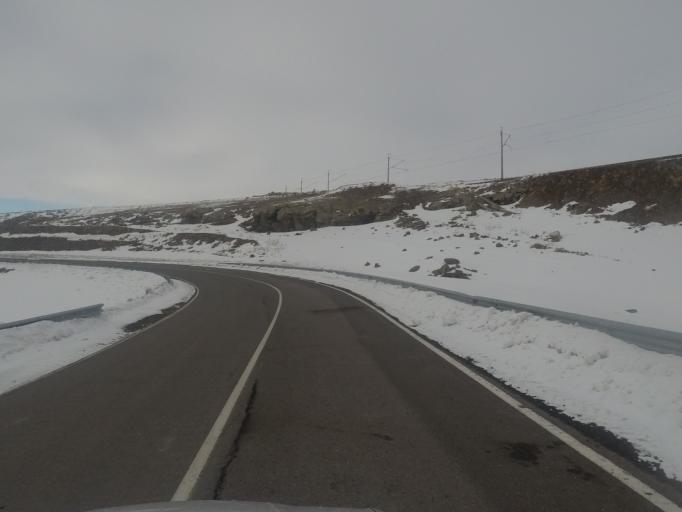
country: GE
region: Kvemo Kartli
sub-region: Tsalka
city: Tsalka
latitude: 41.4427
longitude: 43.8491
